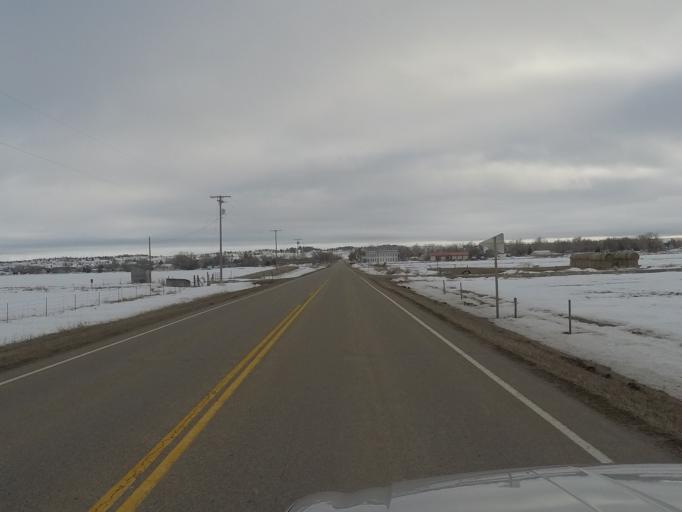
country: US
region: Montana
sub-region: Golden Valley County
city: Ryegate
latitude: 46.2995
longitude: -108.9380
